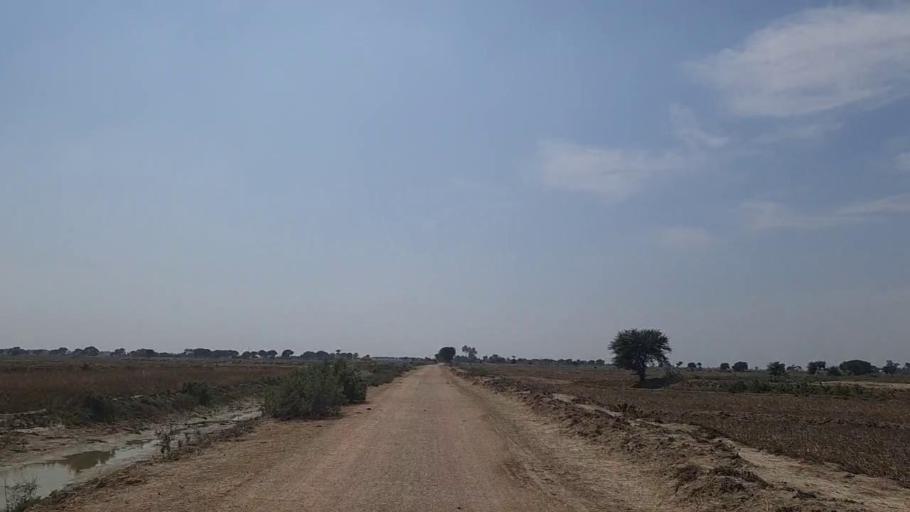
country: PK
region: Sindh
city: Jati
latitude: 24.5369
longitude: 68.3034
